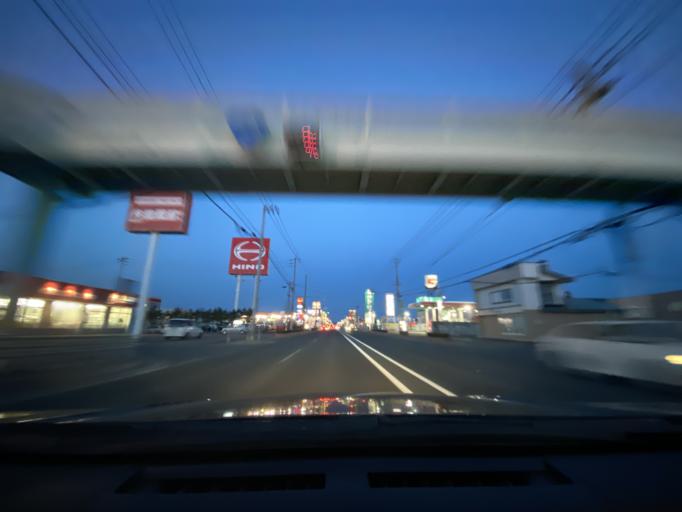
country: JP
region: Hokkaido
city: Kitami
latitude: 43.7974
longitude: 143.8481
